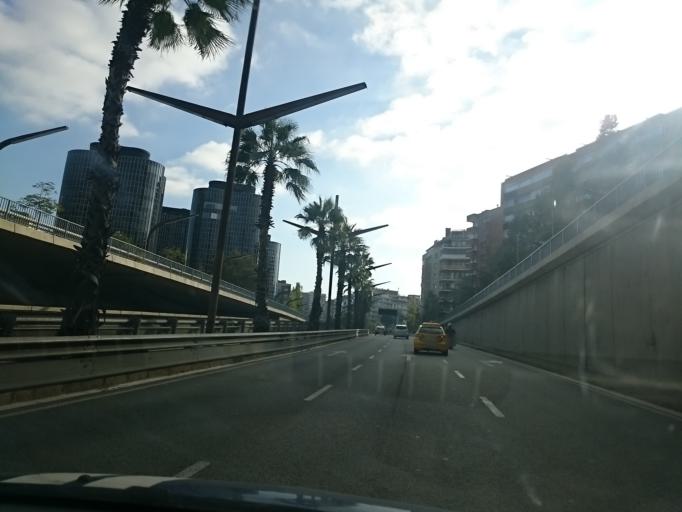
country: ES
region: Catalonia
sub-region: Provincia de Barcelona
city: les Corts
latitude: 41.3875
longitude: 2.1272
